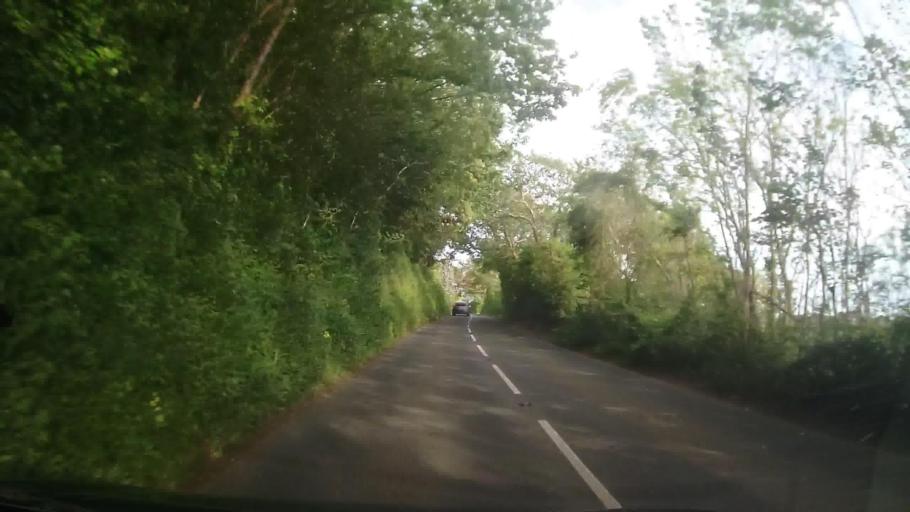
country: GB
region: England
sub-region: Devon
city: Kingsbridge
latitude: 50.2715
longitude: -3.7605
